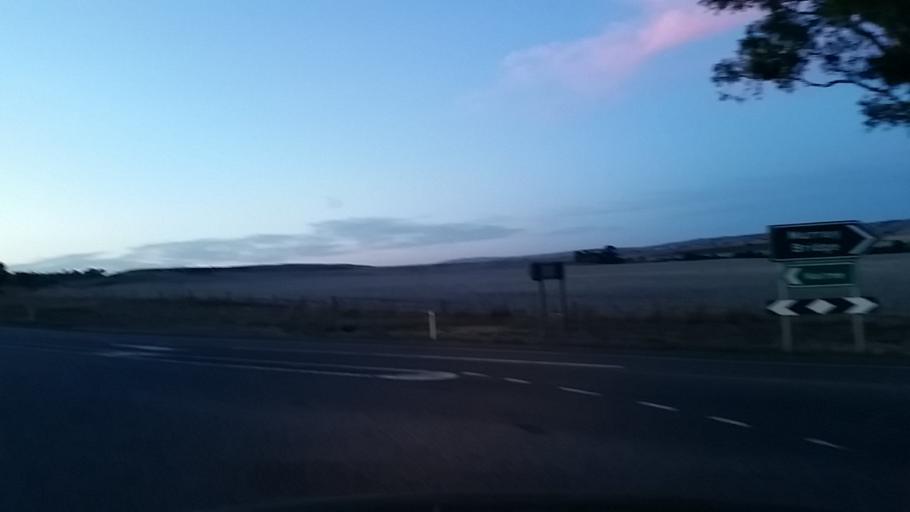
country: AU
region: South Australia
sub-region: Mount Barker
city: Callington
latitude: -35.1075
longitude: 139.0376
